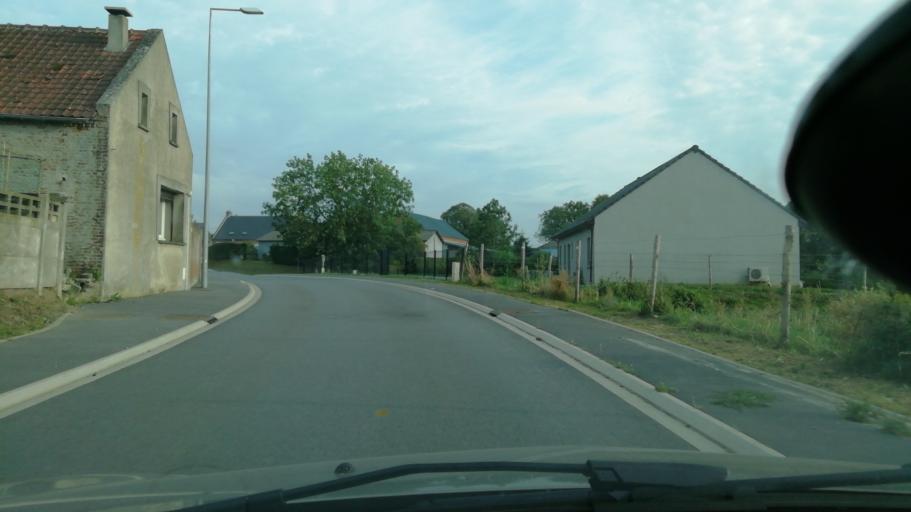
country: FR
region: Nord-Pas-de-Calais
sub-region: Departement du Nord
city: Bertry
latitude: 50.1101
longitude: 3.4706
